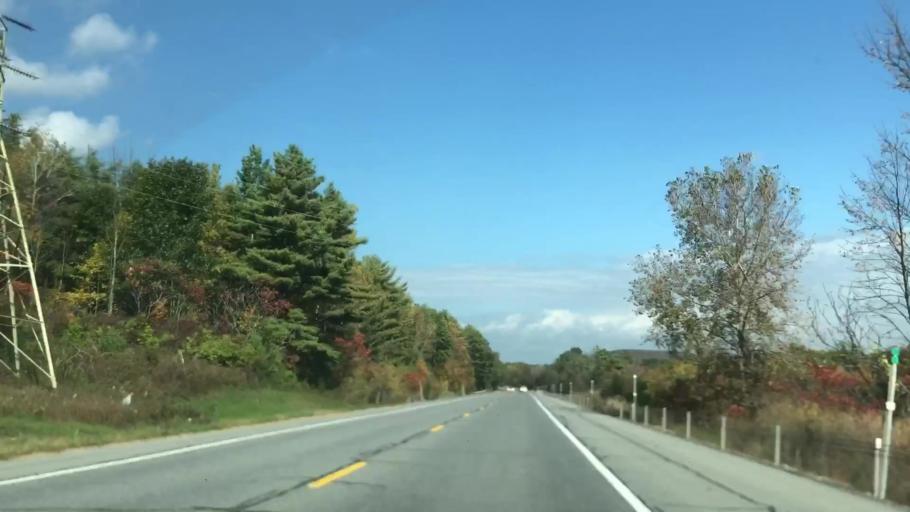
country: US
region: New York
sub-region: Washington County
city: Whitehall
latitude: 43.4398
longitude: -73.4570
